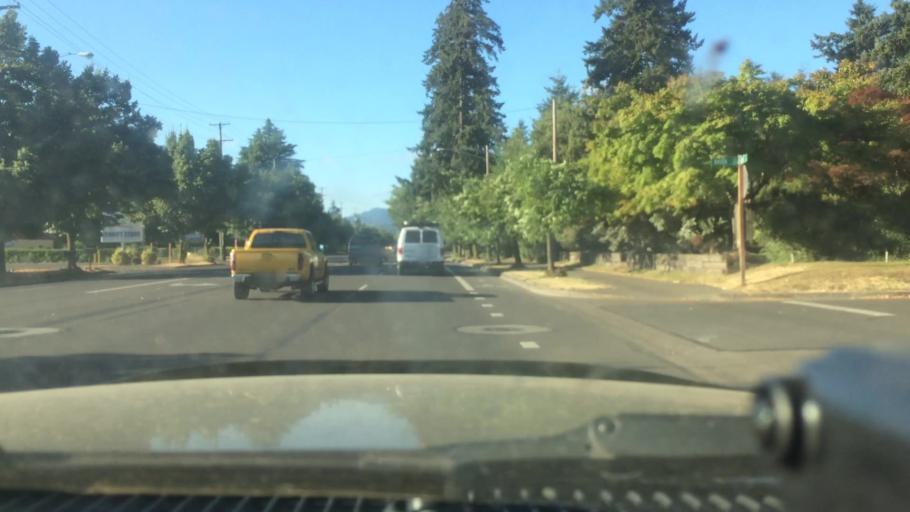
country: US
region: Oregon
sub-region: Lane County
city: Eugene
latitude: 44.0705
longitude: -123.1185
